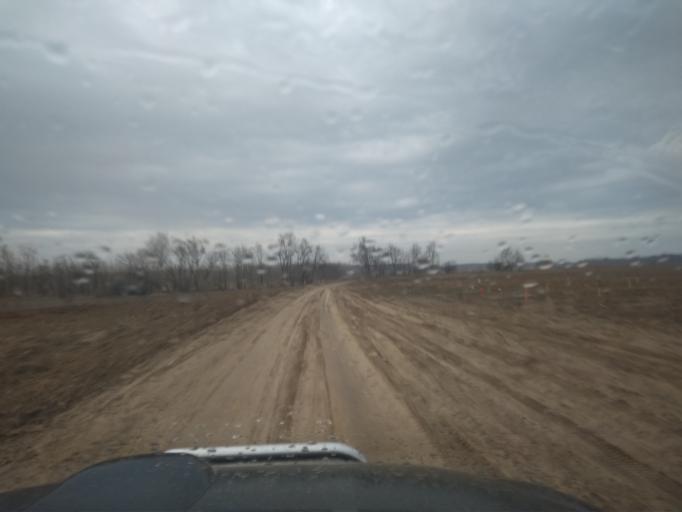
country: HU
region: Szabolcs-Szatmar-Bereg
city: Apagy
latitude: 47.9698
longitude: 21.9213
